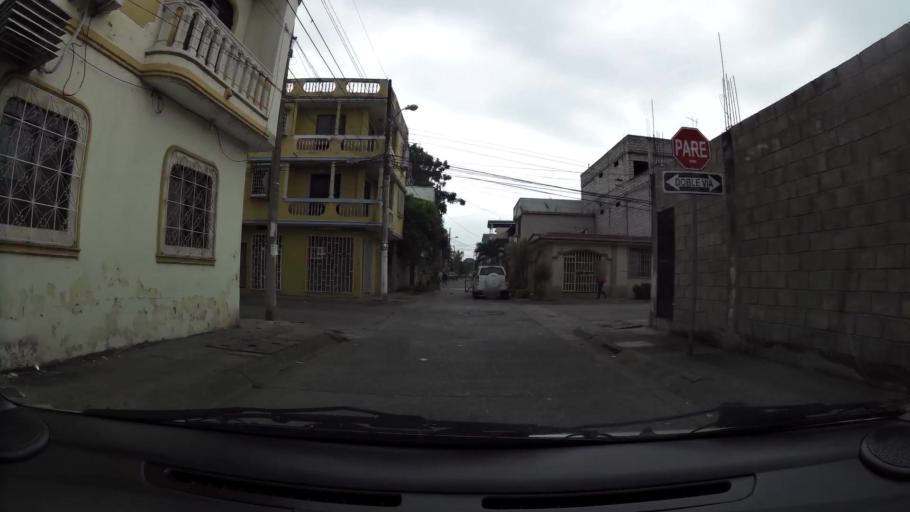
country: EC
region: Guayas
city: Eloy Alfaro
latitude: -2.1212
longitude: -79.8836
